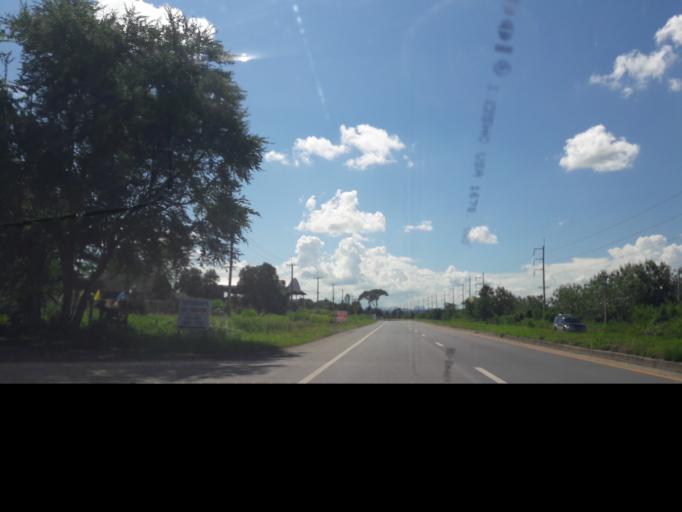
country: TH
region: Kanchanaburi
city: Sai Yok
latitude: 14.0894
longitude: 99.3168
